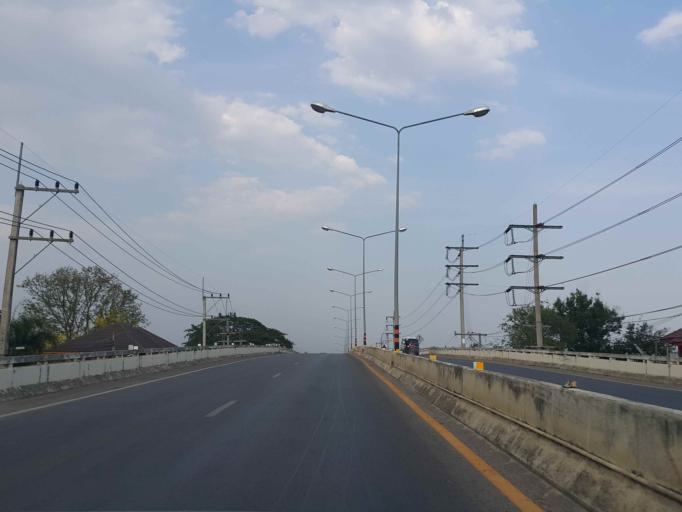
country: TH
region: Chiang Mai
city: San Sai
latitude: 18.9170
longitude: 98.9683
